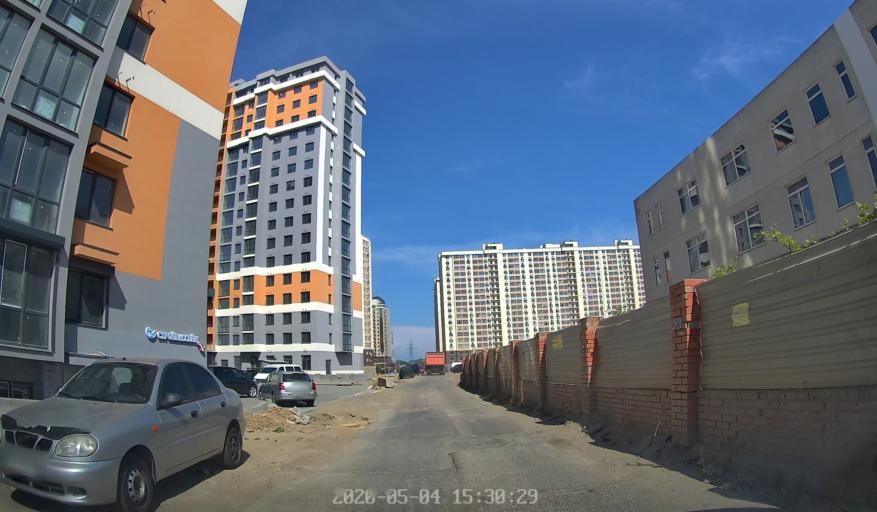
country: NG
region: Niger
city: Lemu
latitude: 9.2761
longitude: 6.1410
